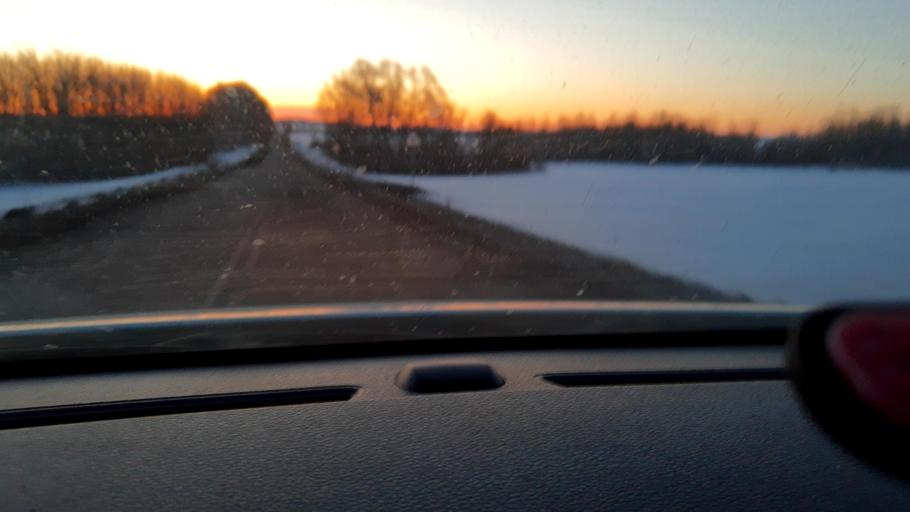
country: RU
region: Bashkortostan
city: Avdon
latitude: 54.3877
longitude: 55.7403
